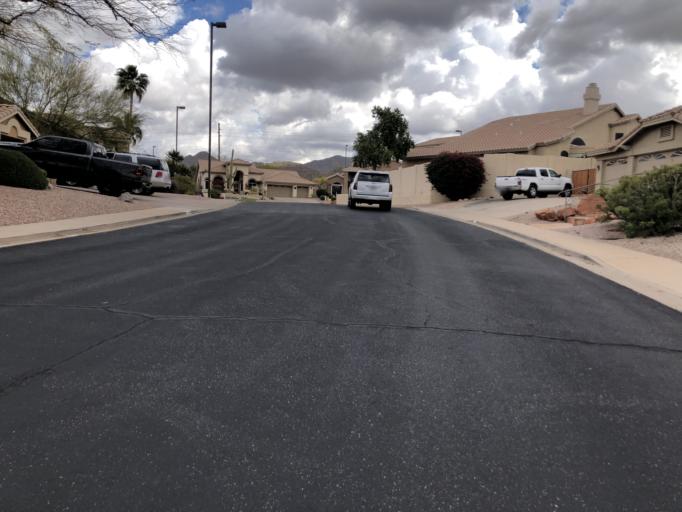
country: US
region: Arizona
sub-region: Maricopa County
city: Fountain Hills
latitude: 33.4905
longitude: -111.6856
